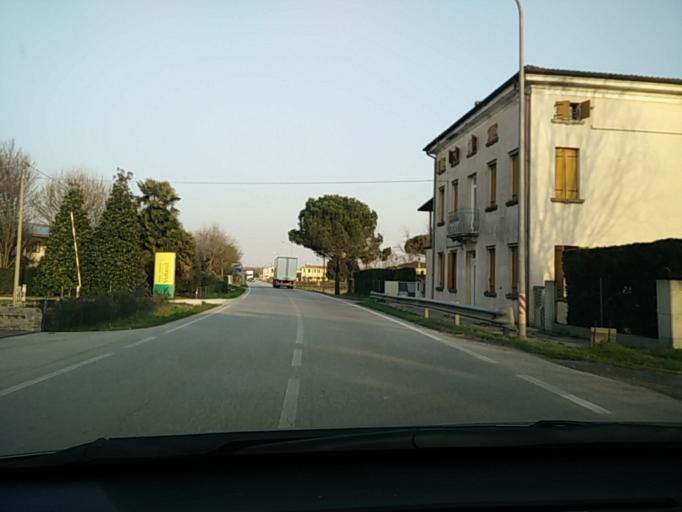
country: IT
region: Veneto
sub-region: Provincia di Treviso
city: Candelu
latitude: 45.7318
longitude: 12.3813
